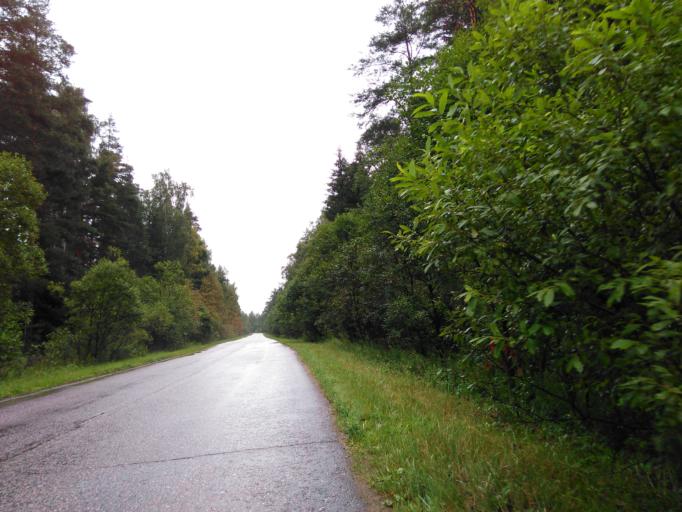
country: RU
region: Moskovskaya
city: Elektrogorsk
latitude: 55.9445
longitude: 38.6562
